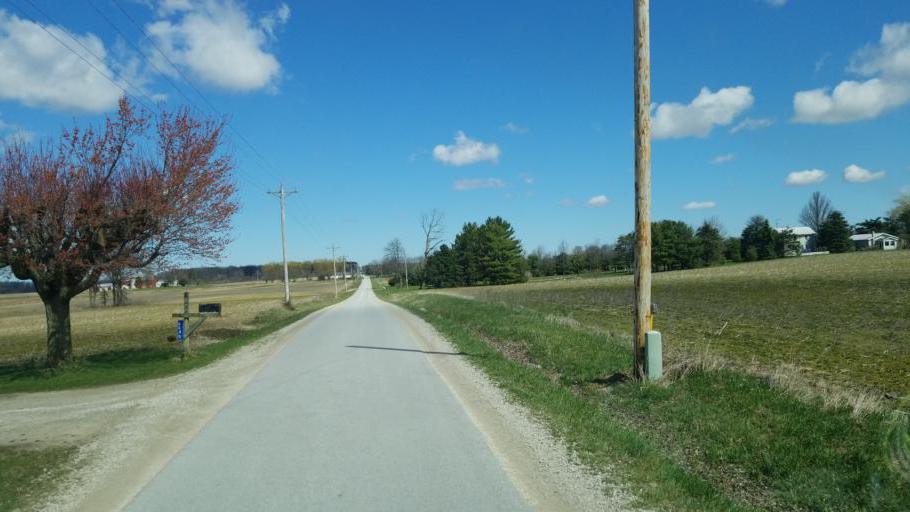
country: US
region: Ohio
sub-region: Sandusky County
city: Mount Carmel
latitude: 41.2216
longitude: -82.9372
